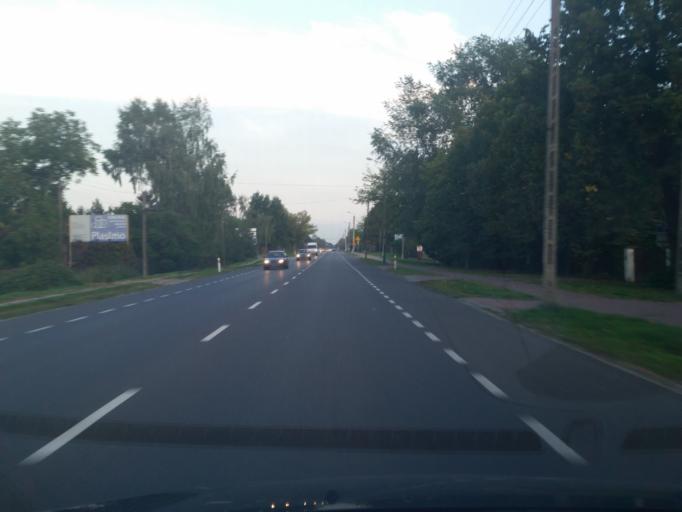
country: PL
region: Masovian Voivodeship
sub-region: Powiat legionowski
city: Jablonna
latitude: 52.3873
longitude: 20.8937
